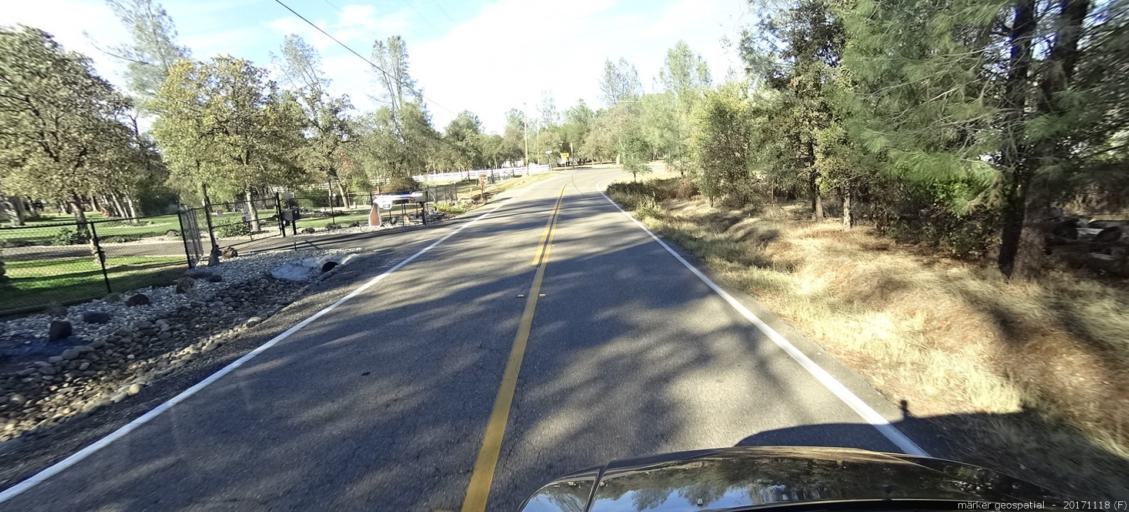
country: US
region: California
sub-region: Shasta County
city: Redding
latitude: 40.4842
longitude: -122.4549
